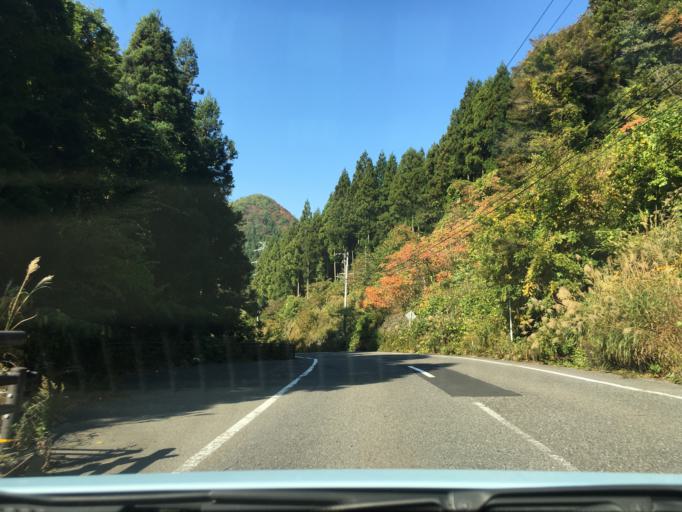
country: JP
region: Fukushima
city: Sukagawa
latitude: 37.3001
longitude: 140.1570
